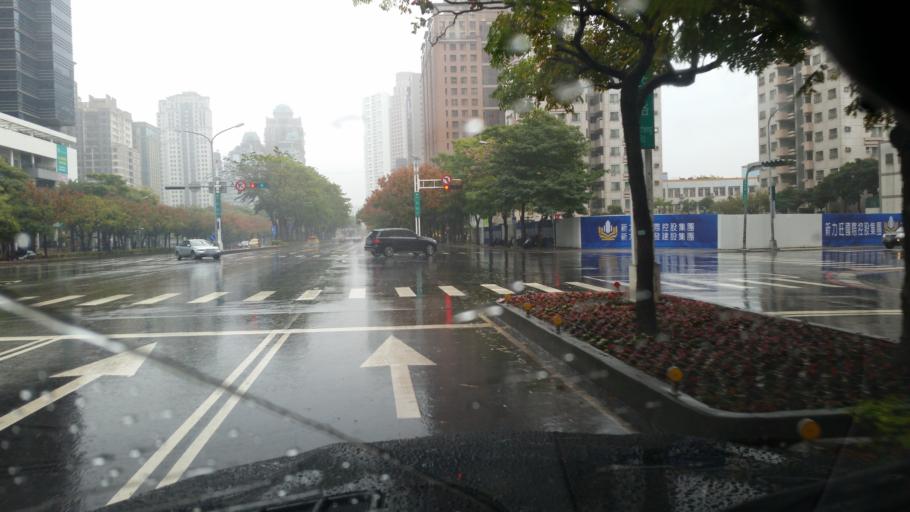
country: TW
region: Taiwan
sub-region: Taichung City
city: Taichung
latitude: 24.1590
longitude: 120.6387
